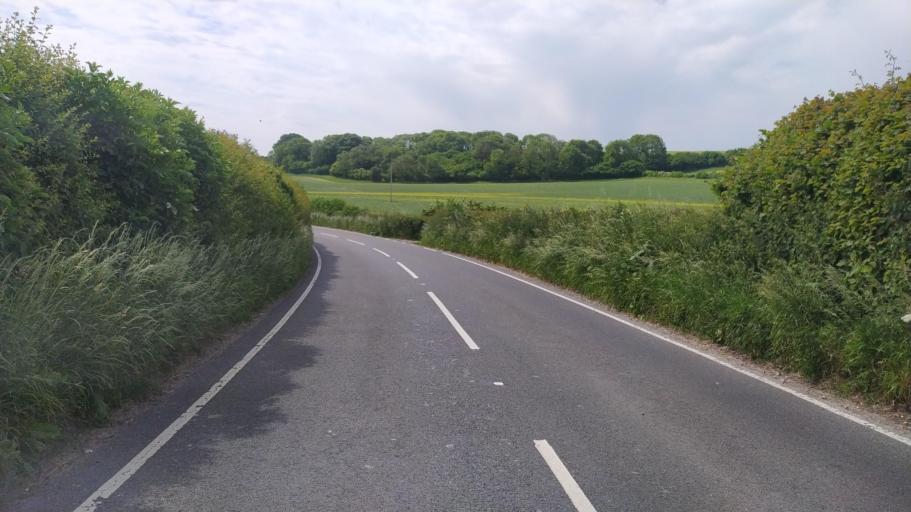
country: GB
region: England
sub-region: Dorset
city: Dorchester
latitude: 50.7925
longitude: -2.4784
